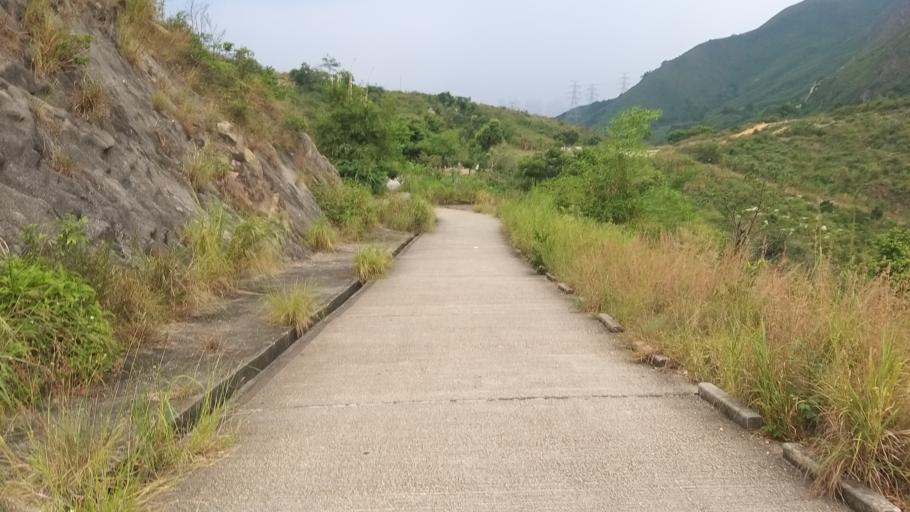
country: HK
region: Tuen Mun
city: Tuen Mun
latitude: 22.4083
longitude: 113.9524
